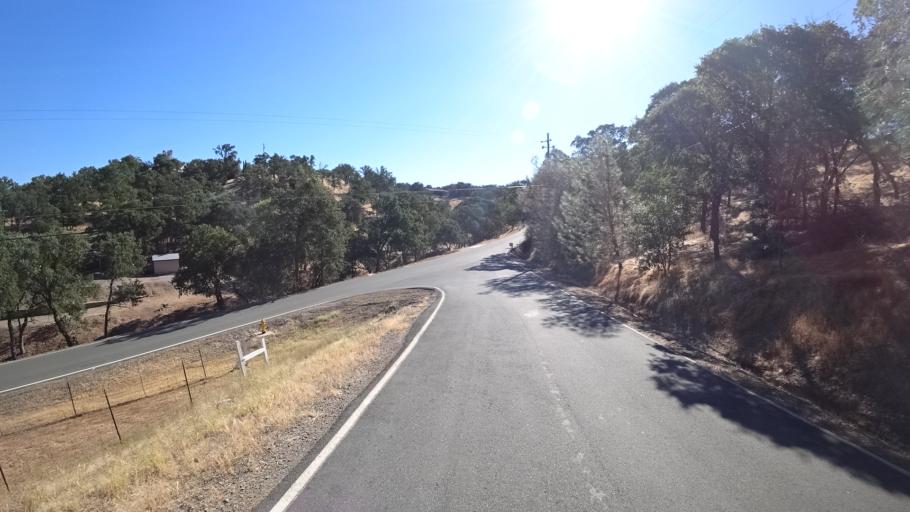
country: US
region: California
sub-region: Calaveras County
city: Rancho Calaveras
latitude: 38.1210
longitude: -120.8720
